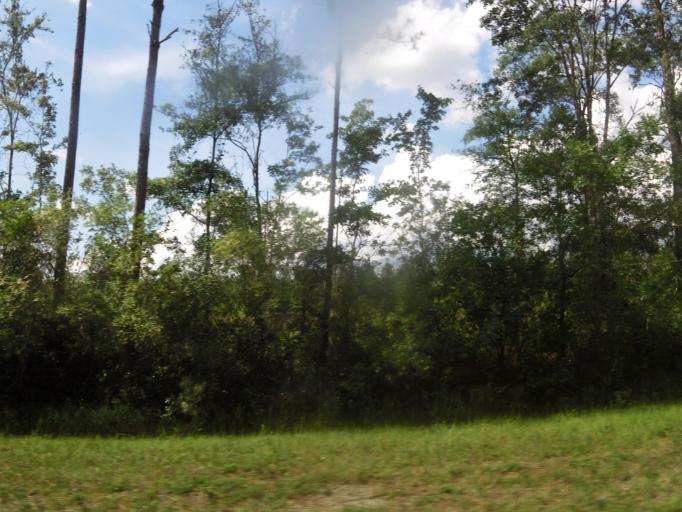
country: US
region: Florida
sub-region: Duval County
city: Baldwin
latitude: 30.2018
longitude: -82.0227
